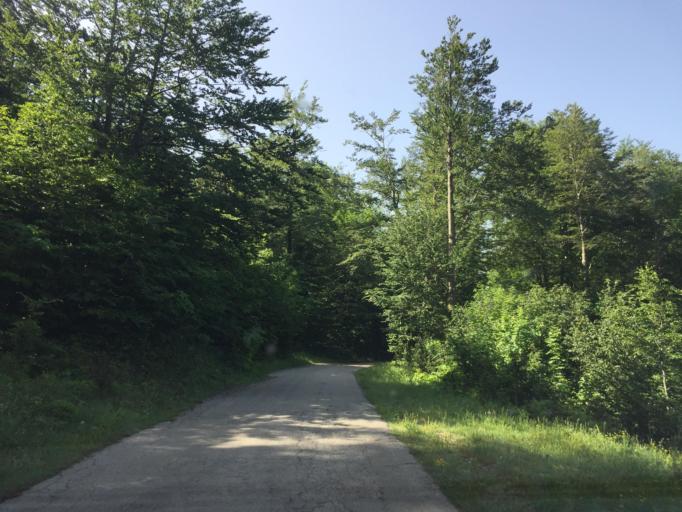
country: HR
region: Primorsko-Goranska
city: Podhum
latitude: 45.4361
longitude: 14.5631
